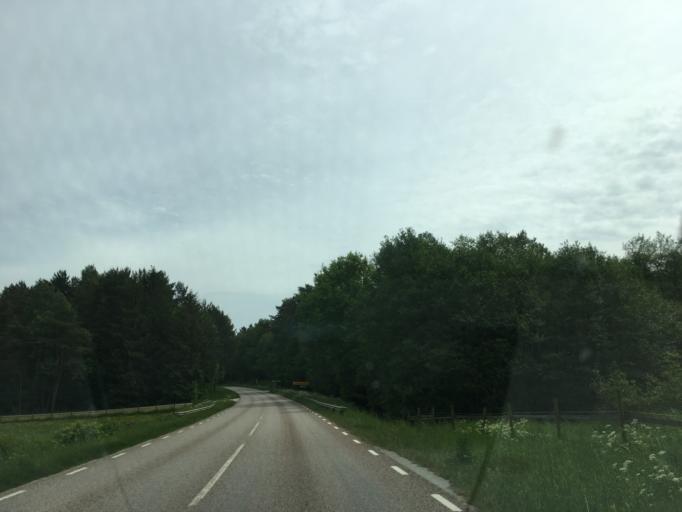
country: SE
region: Skane
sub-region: Lunds Kommun
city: Veberod
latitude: 55.6251
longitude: 13.5337
